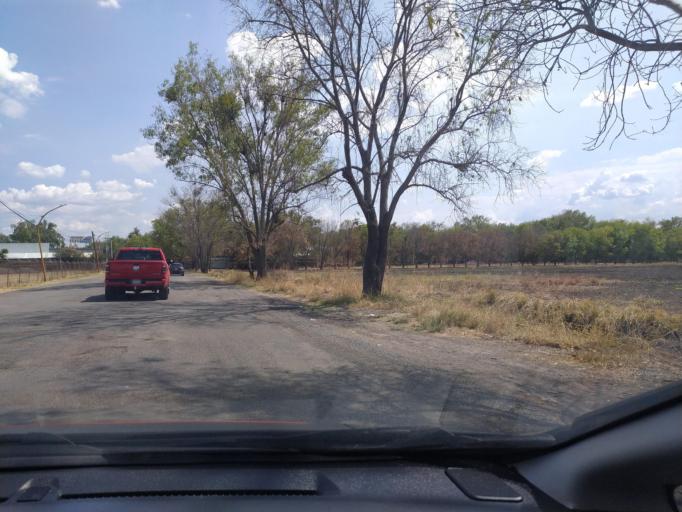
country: MX
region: Guanajuato
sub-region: San Francisco del Rincon
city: Estacion de San Francisco
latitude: 21.0292
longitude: -101.8397
